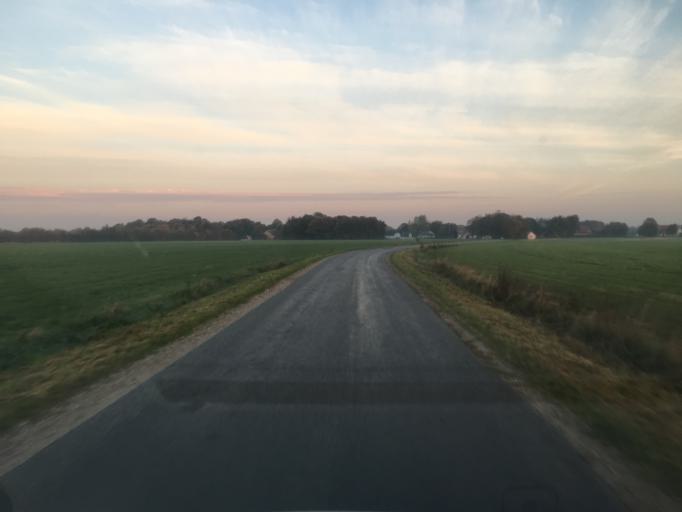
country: DK
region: South Denmark
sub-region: Tonder Kommune
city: Logumkloster
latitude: 54.9965
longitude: 9.0472
